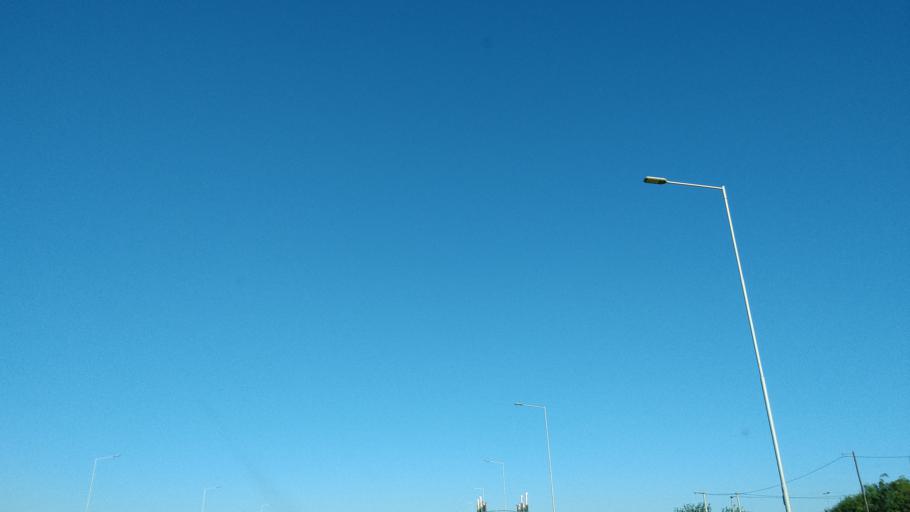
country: AR
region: Cordoba
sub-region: Departamento de Capital
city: Cordoba
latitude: -31.3606
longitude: -64.1587
